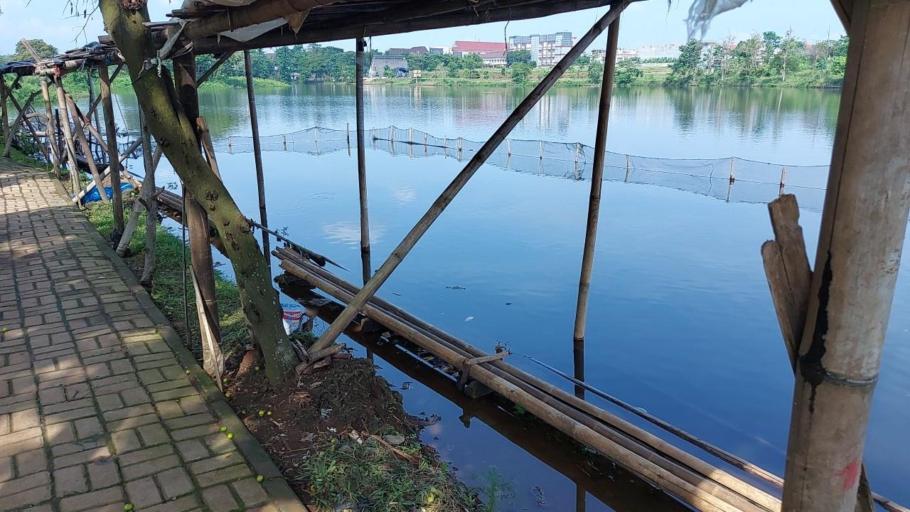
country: ID
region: West Java
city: Cibinong
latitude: -6.4709
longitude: 106.8350
